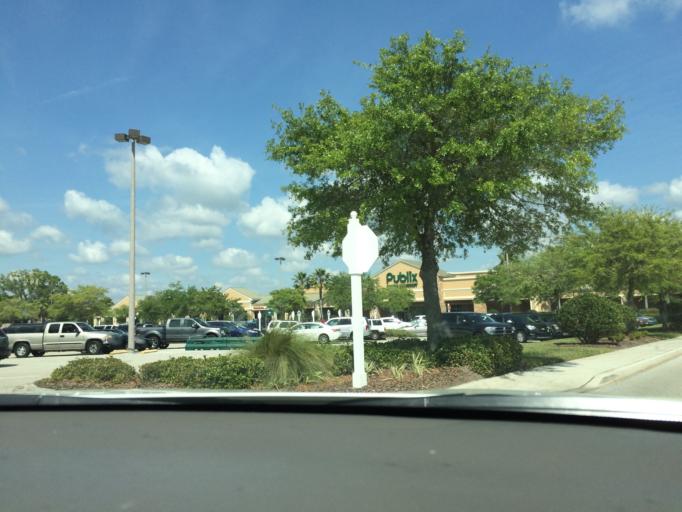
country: US
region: Florida
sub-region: Manatee County
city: Ellenton
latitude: 27.4829
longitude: -82.4330
